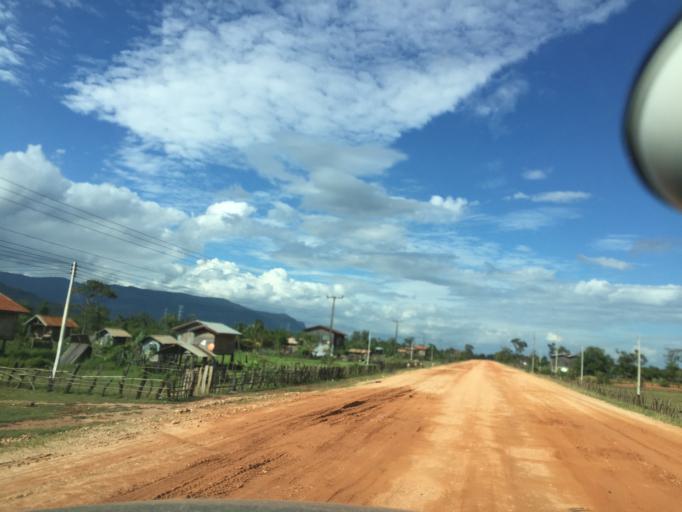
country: LA
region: Attapu
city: Attapu
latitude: 14.6924
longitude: 106.6098
